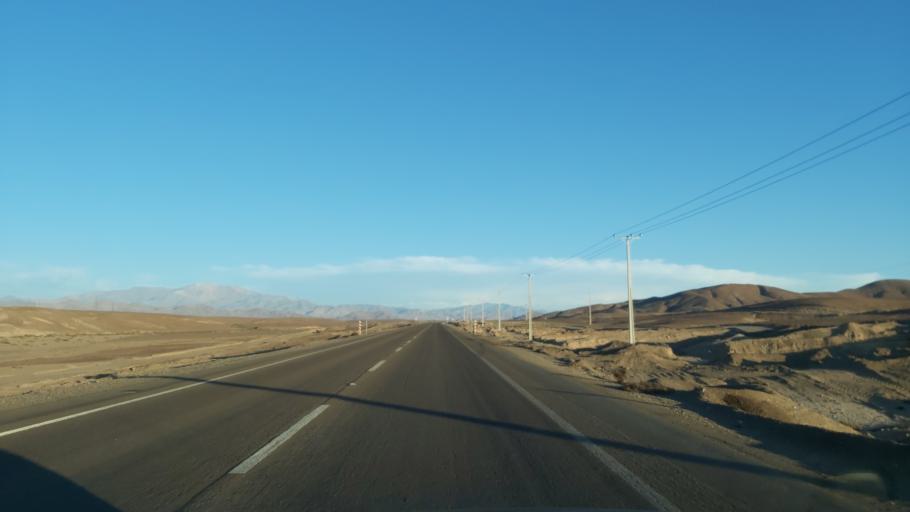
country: CL
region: Atacama
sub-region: Provincia de Chanaral
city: Diego de Almagro
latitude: -26.4318
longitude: -70.0096
